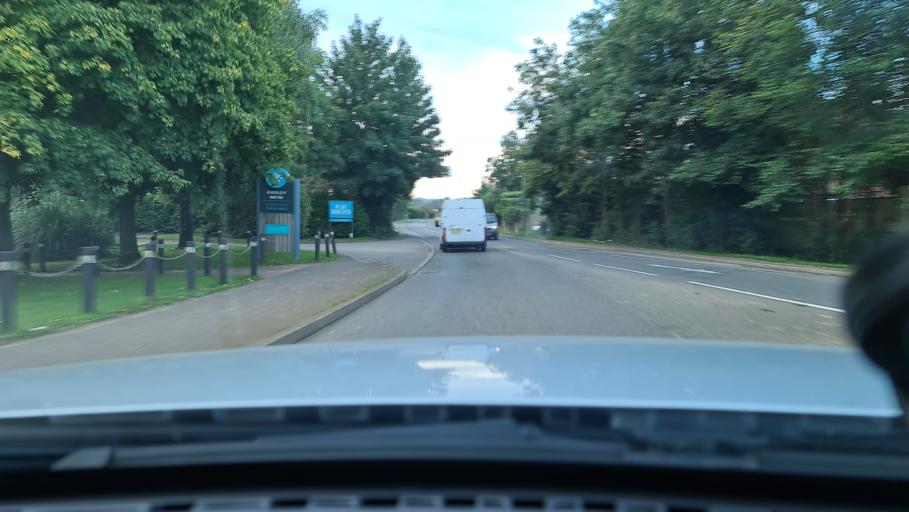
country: GB
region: England
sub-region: Oxfordshire
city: Hanwell
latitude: 52.0712
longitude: -1.3632
